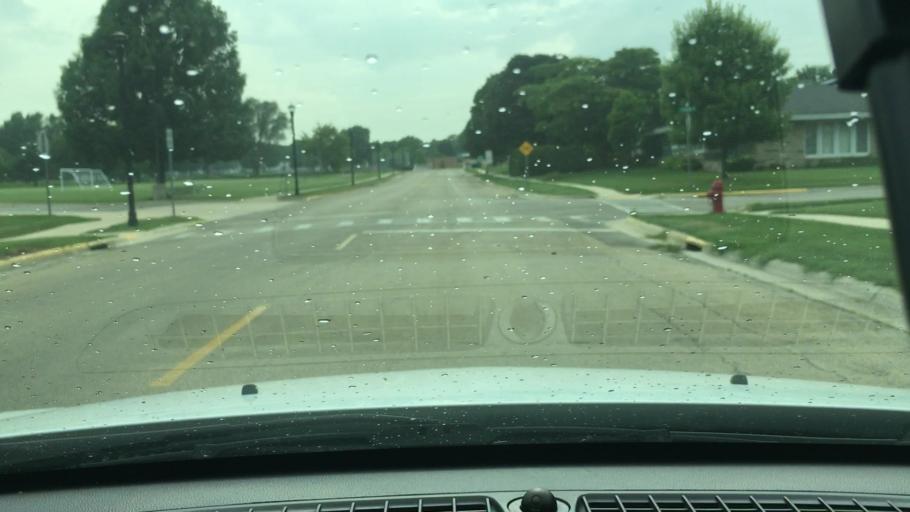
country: US
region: Illinois
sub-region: Ogle County
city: Rochelle
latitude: 41.9307
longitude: -89.0577
